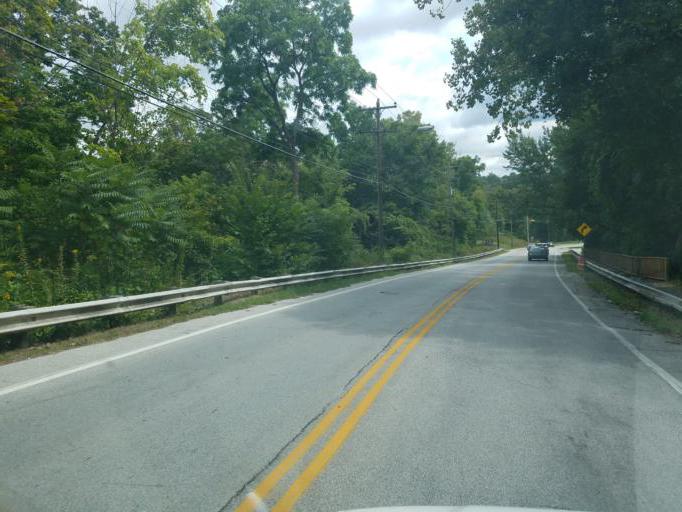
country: US
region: Ohio
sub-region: Lake County
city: Painesville
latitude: 41.7200
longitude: -81.2313
